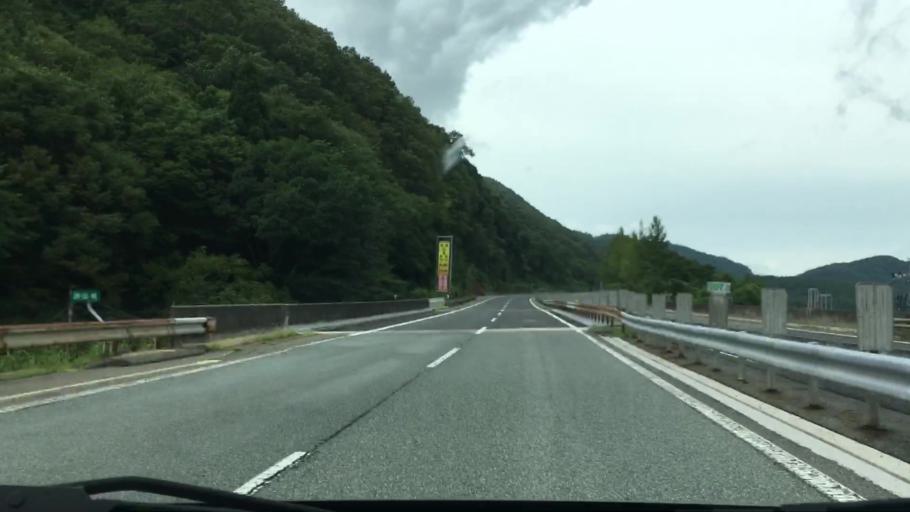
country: JP
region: Okayama
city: Niimi
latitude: 34.9716
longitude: 133.6249
